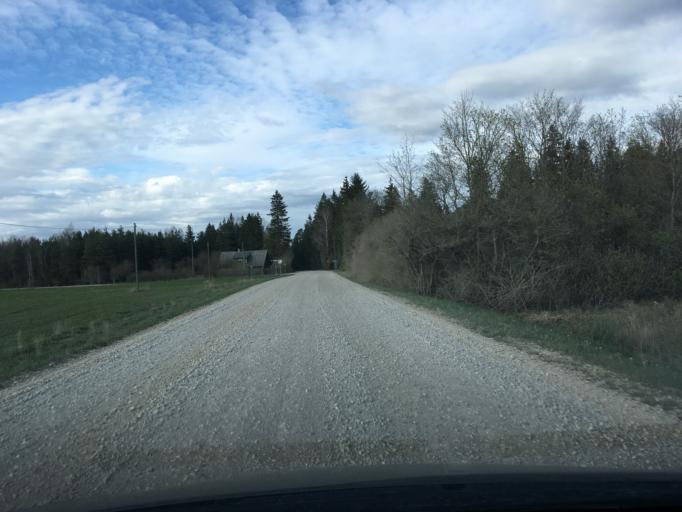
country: EE
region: Raplamaa
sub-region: Maerjamaa vald
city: Marjamaa
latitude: 58.9495
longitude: 24.3210
